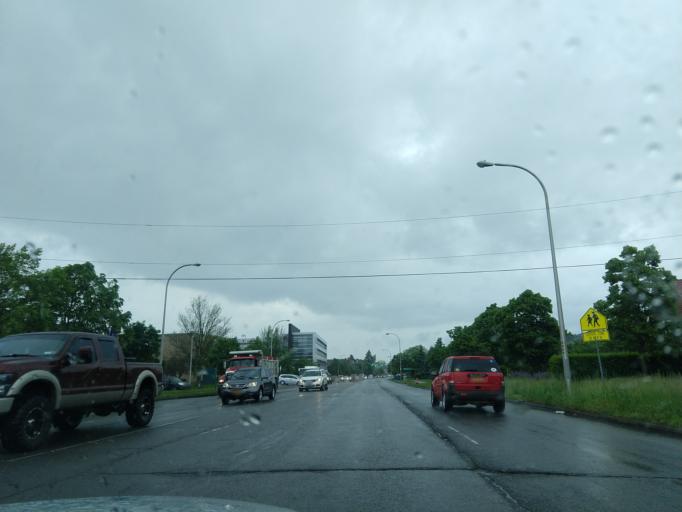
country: US
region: New York
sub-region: Erie County
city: Kenmore
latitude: 42.9362
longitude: -78.8782
